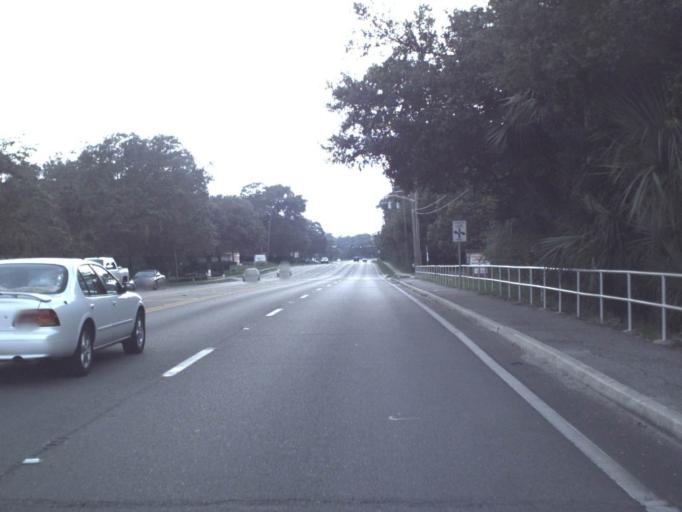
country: US
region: Florida
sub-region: Duval County
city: Jacksonville
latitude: 30.3130
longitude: -81.5877
